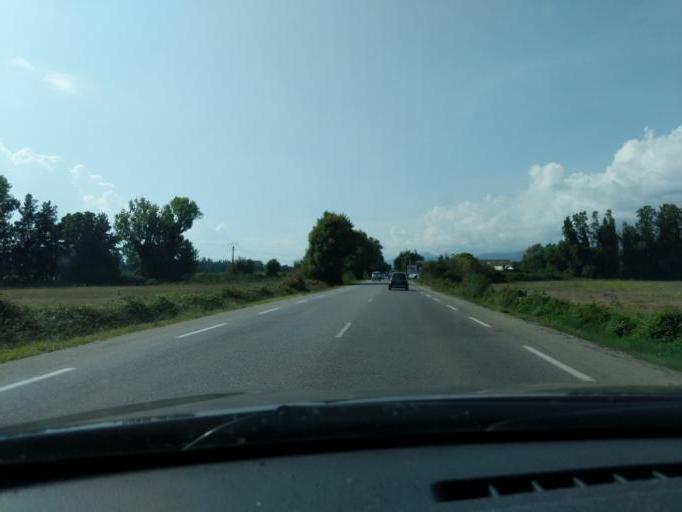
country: FR
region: Corsica
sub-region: Departement de la Haute-Corse
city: Ghisonaccia
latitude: 41.9752
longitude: 9.3993
